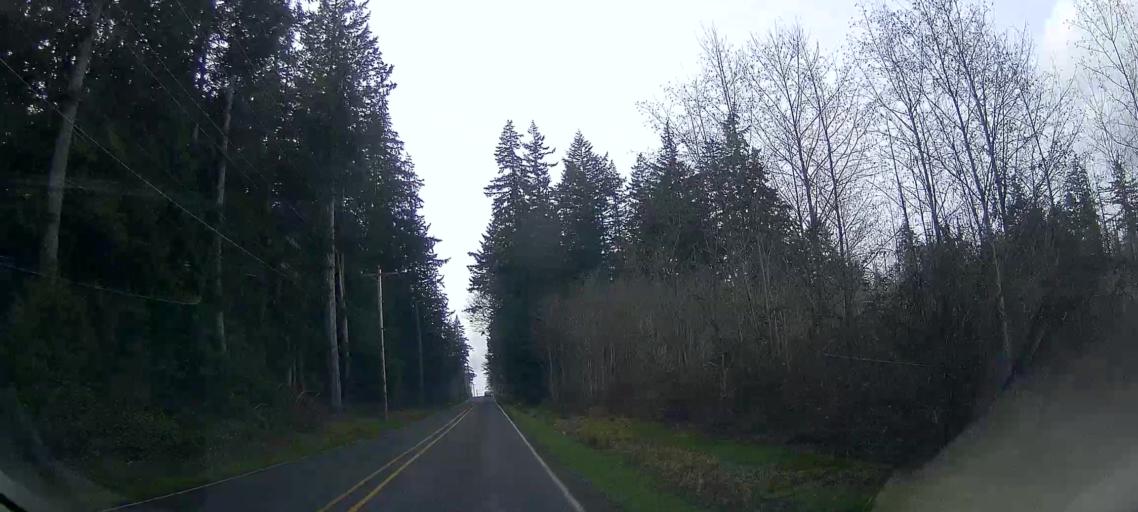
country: US
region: Washington
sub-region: Island County
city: Camano
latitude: 48.1384
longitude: -122.4888
